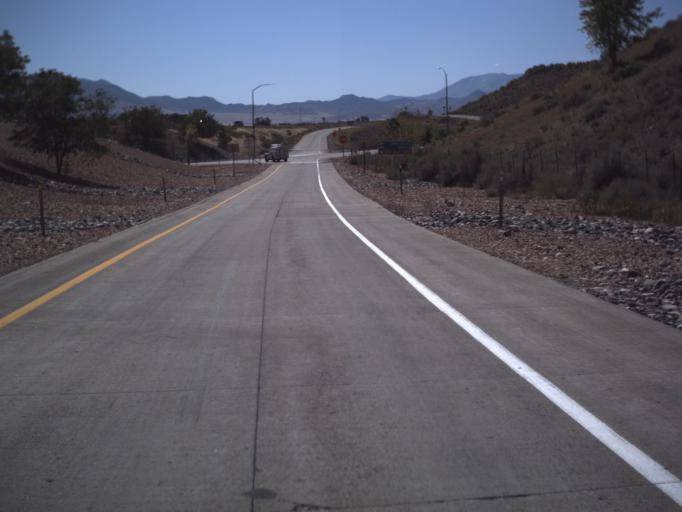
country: US
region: Utah
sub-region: Sevier County
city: Richfield
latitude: 38.7519
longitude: -112.1059
